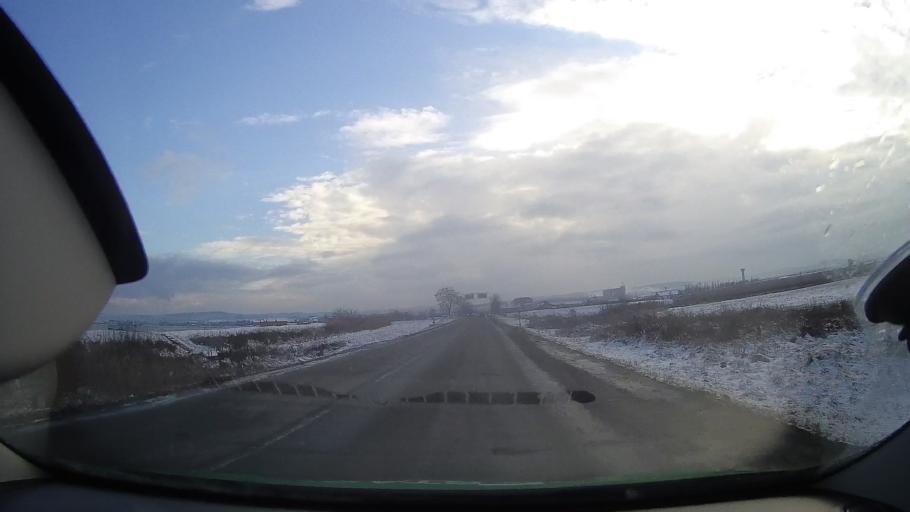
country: RO
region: Mures
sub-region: Comuna Iernut
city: Iernut
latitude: 46.4439
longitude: 24.2514
